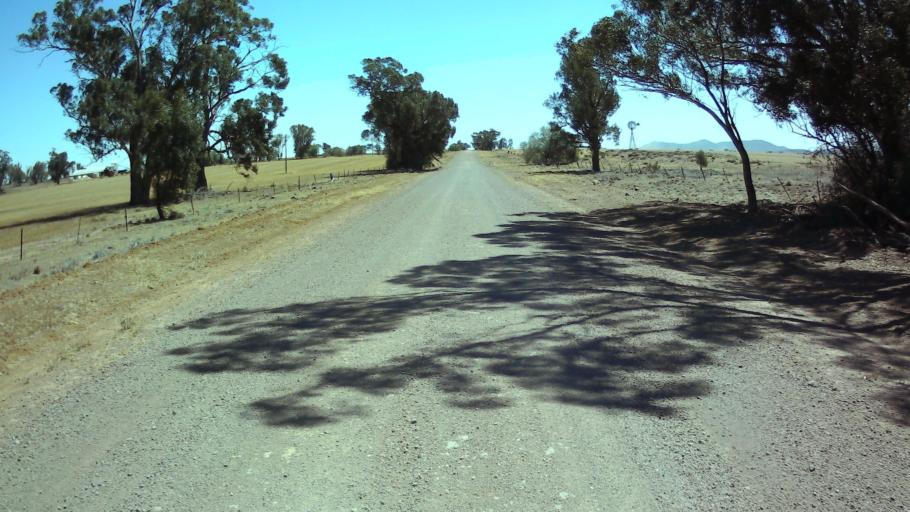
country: AU
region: New South Wales
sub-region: Forbes
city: Forbes
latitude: -33.6994
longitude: 147.7069
